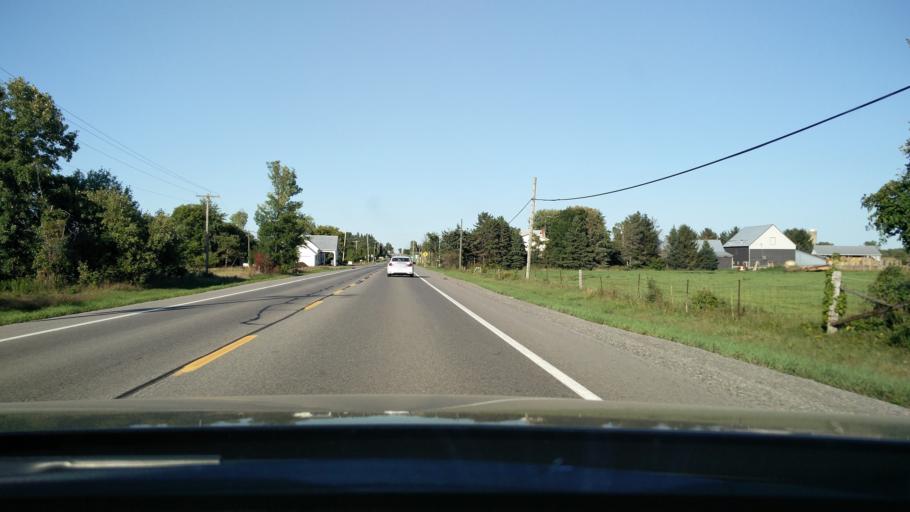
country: CA
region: Ontario
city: Bells Corners
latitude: 45.1434
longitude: -75.9194
